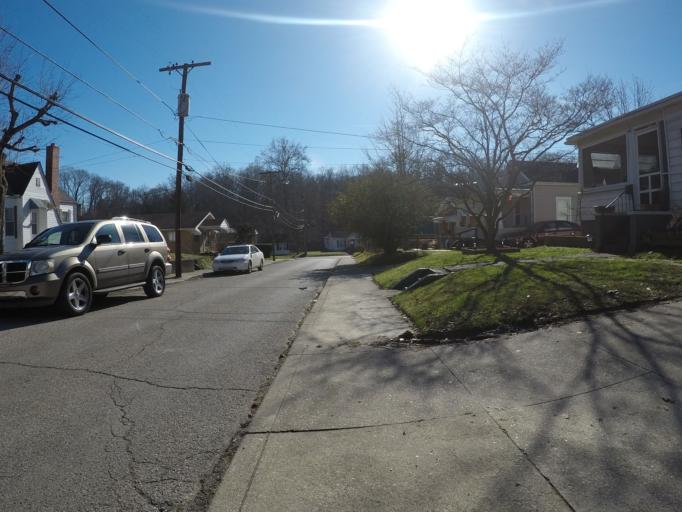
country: US
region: West Virginia
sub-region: Cabell County
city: Huntington
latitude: 38.4102
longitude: -82.3982
